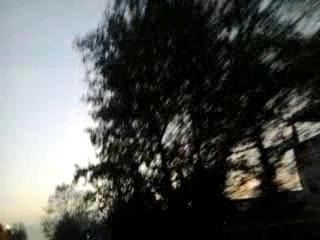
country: IT
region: Lombardy
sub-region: Provincia di Brescia
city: Capriano del Colle
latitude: 45.4832
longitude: 10.1456
